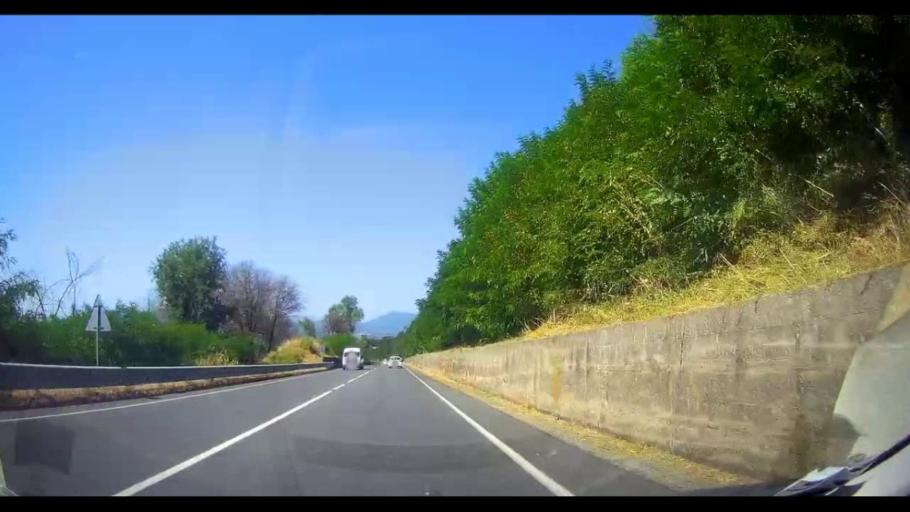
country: IT
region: Calabria
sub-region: Provincia di Cosenza
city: Rovito
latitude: 39.3001
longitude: 16.3129
